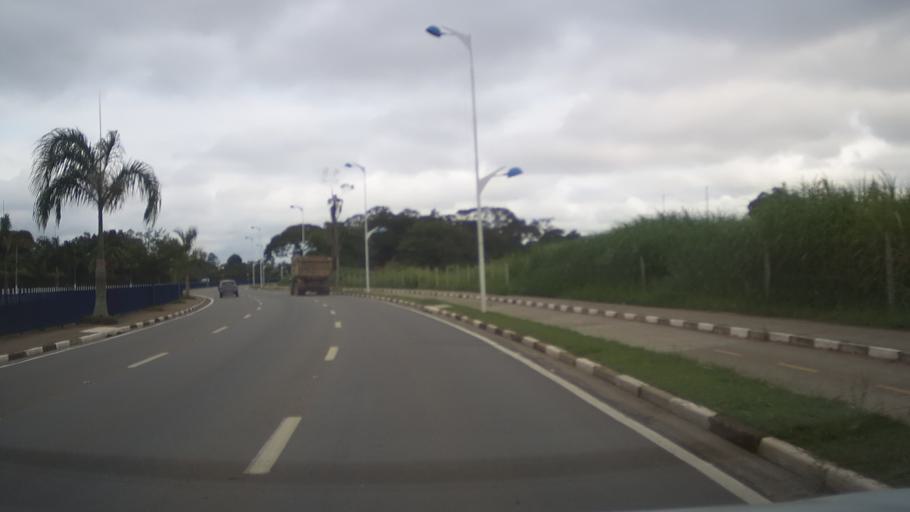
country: BR
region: Sao Paulo
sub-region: Aruja
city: Aruja
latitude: -23.4139
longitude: -46.3703
